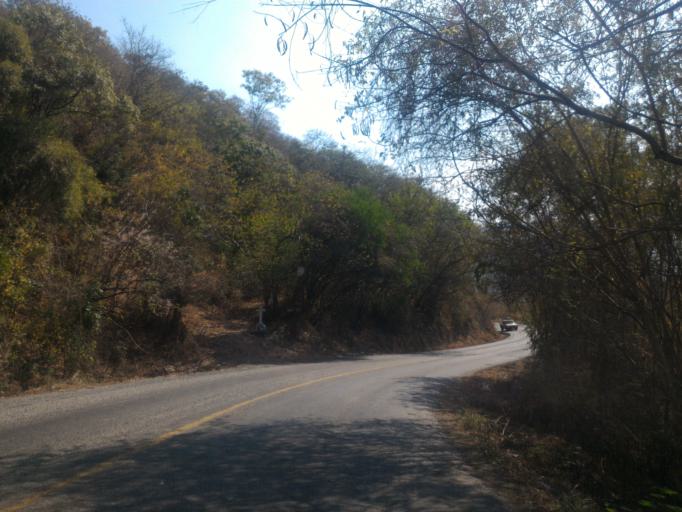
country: MX
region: Michoacan
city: Coahuayana Viejo
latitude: 18.5651
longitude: -103.6349
